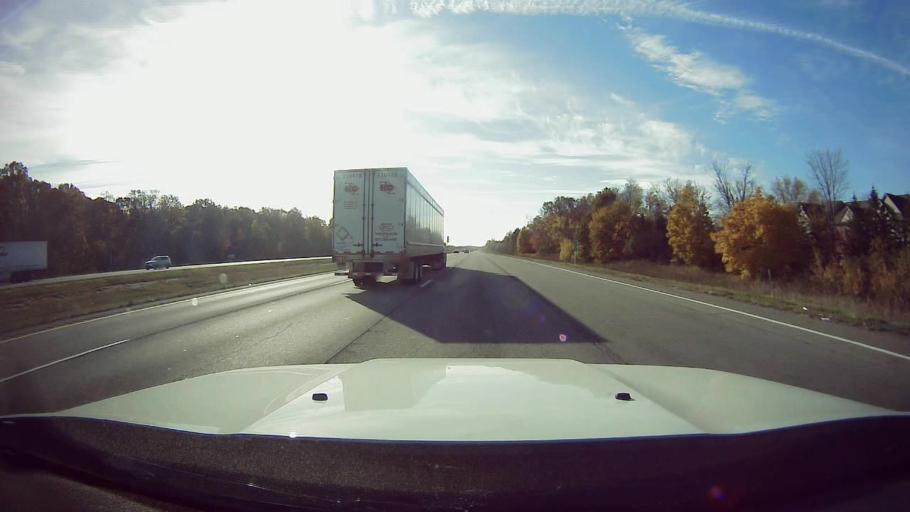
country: US
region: Michigan
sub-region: Wayne County
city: Canton
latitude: 42.3170
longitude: -83.4434
